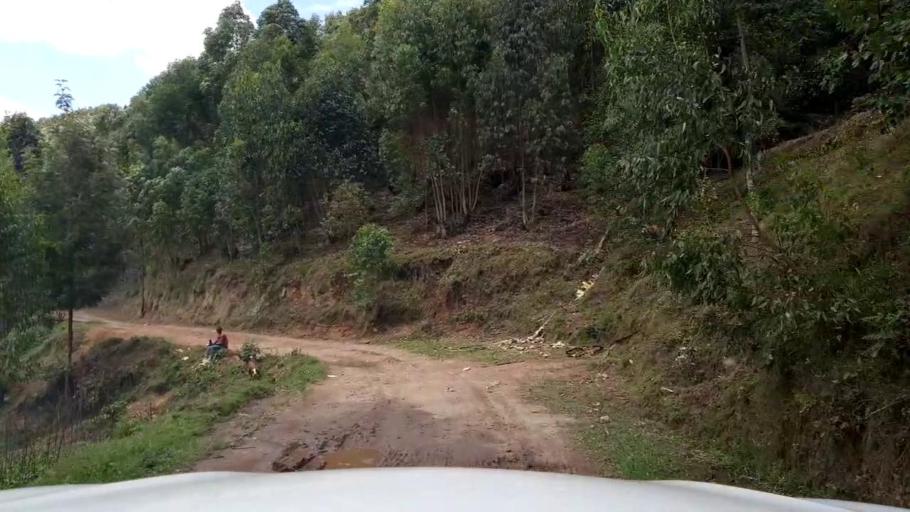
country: RW
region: Northern Province
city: Byumba
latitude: -1.5241
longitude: 30.1306
